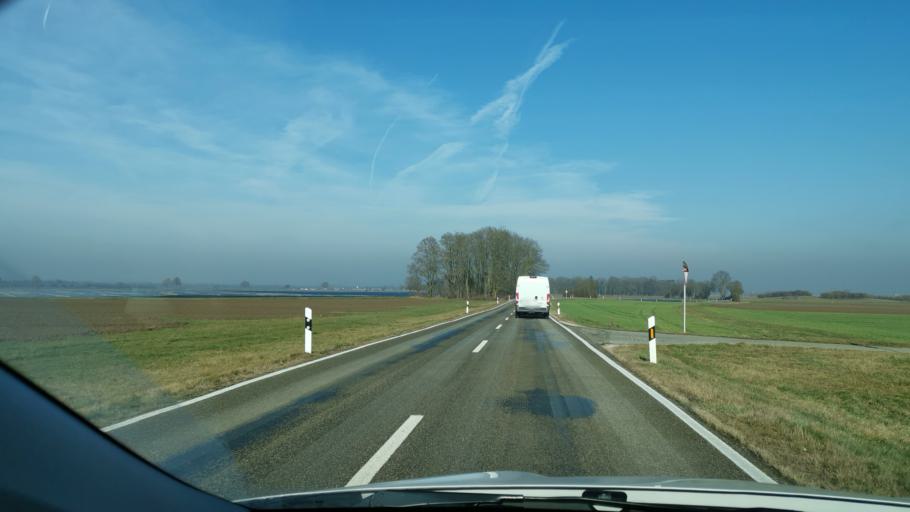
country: DE
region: Bavaria
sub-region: Swabia
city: Munster
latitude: 48.6326
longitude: 10.9263
